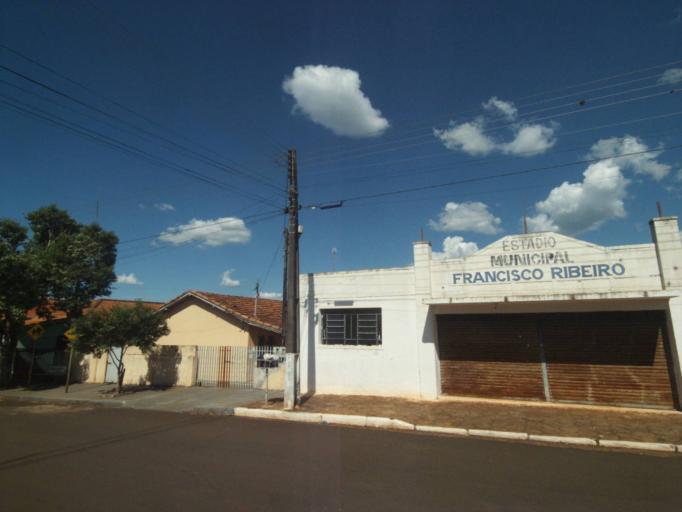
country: BR
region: Parana
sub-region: Sertanopolis
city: Sertanopolis
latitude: -23.0393
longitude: -50.8147
